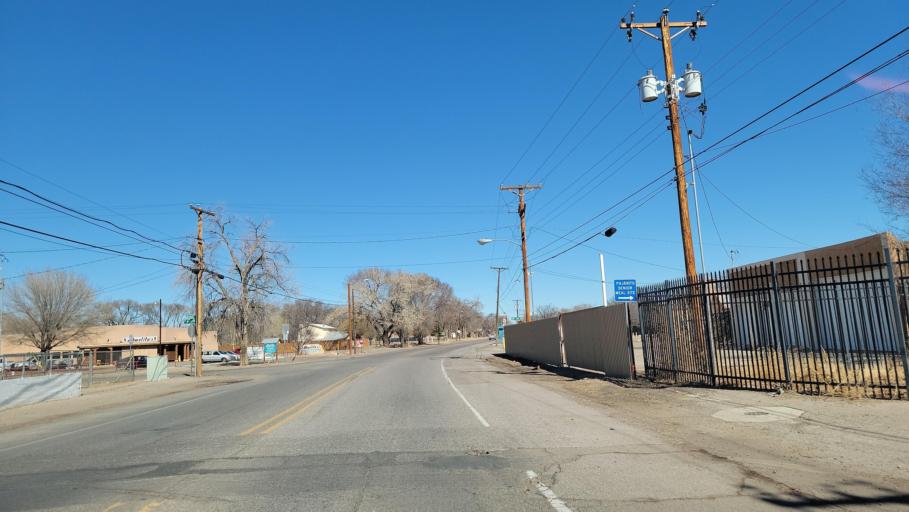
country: US
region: New Mexico
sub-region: Bernalillo County
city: South Valley
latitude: 34.9863
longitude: -106.6966
